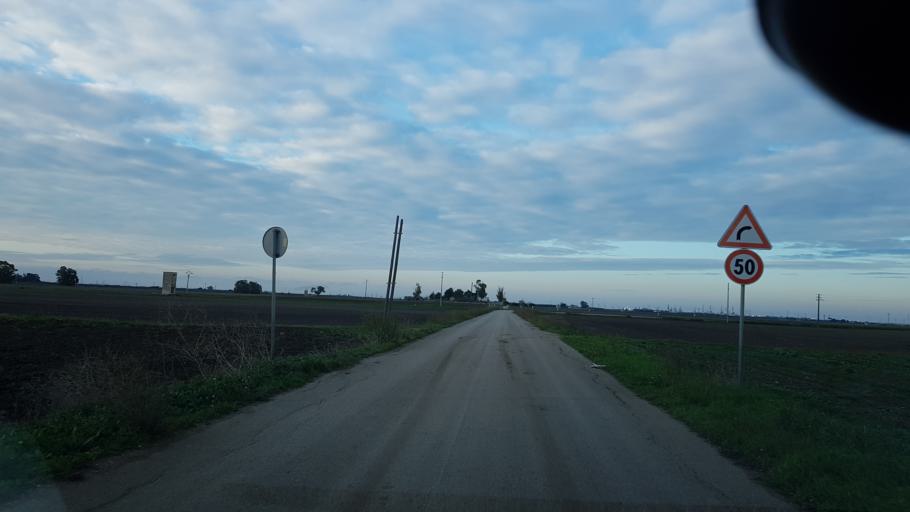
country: IT
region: Apulia
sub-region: Provincia di Brindisi
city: La Rosa
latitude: 40.5724
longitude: 18.0146
